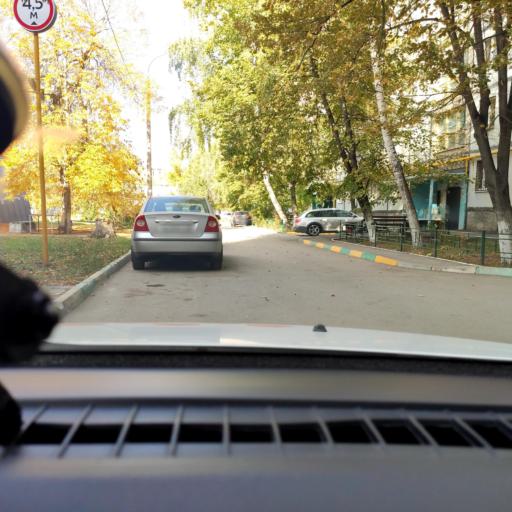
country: RU
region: Samara
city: Samara
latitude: 53.2585
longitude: 50.2318
